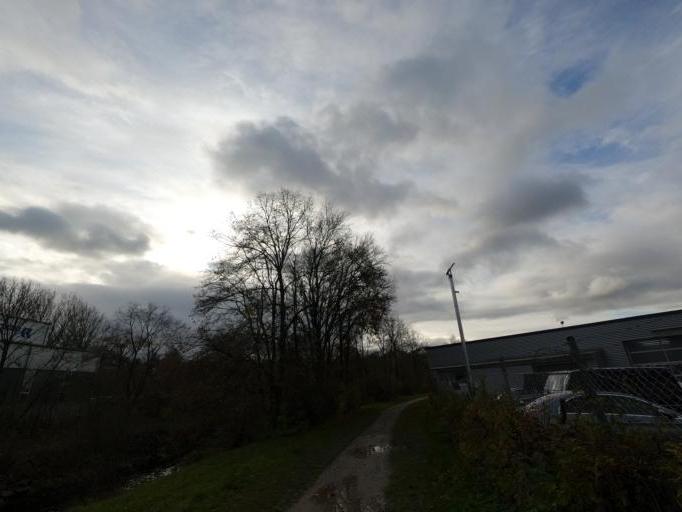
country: DE
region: Baden-Wuerttemberg
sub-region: Regierungsbezirk Stuttgart
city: Wangen
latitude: 48.7058
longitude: 9.6098
